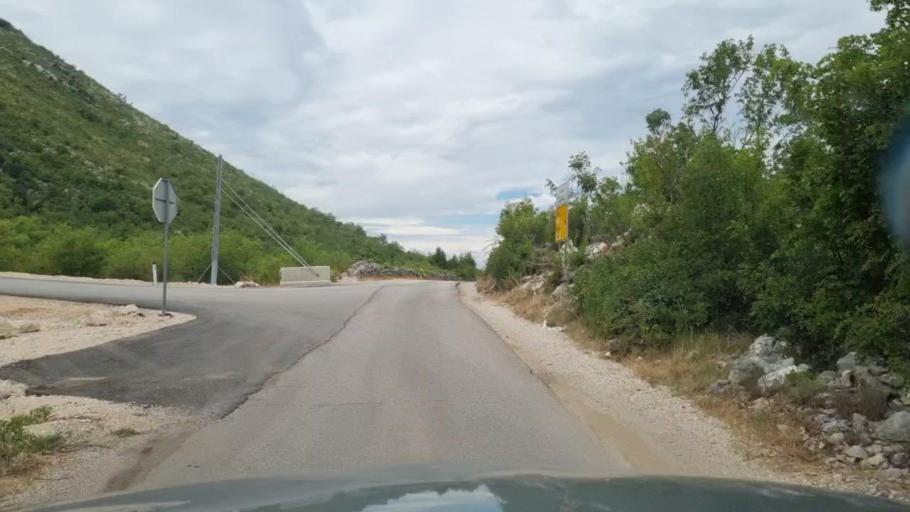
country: HR
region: Dubrovacko-Neretvanska
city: Podgora
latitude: 42.9690
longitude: 17.7935
